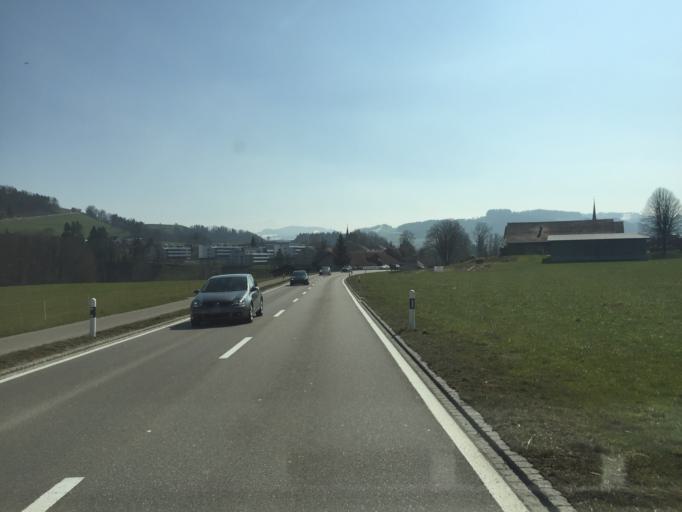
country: CH
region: Saint Gallen
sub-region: Wahlkreis Toggenburg
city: Lutisburg
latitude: 47.3987
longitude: 9.0743
